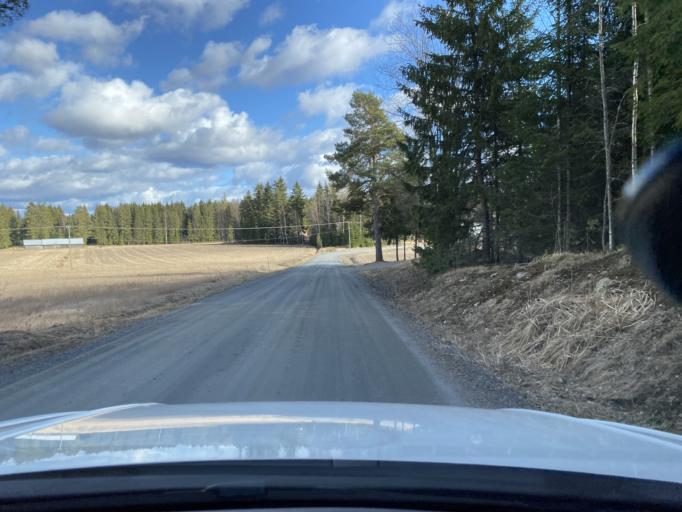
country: FI
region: Pirkanmaa
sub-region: Lounais-Pirkanmaa
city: Punkalaidun
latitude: 61.0946
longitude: 23.2267
